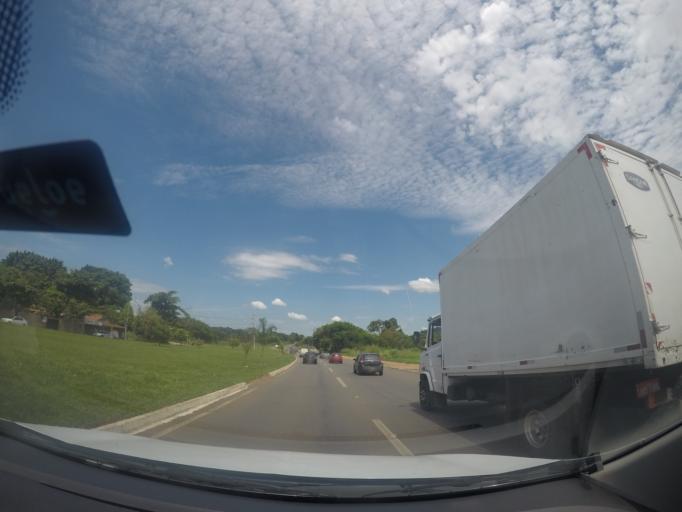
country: BR
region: Goias
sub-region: Goiania
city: Goiania
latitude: -16.6824
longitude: -49.3336
